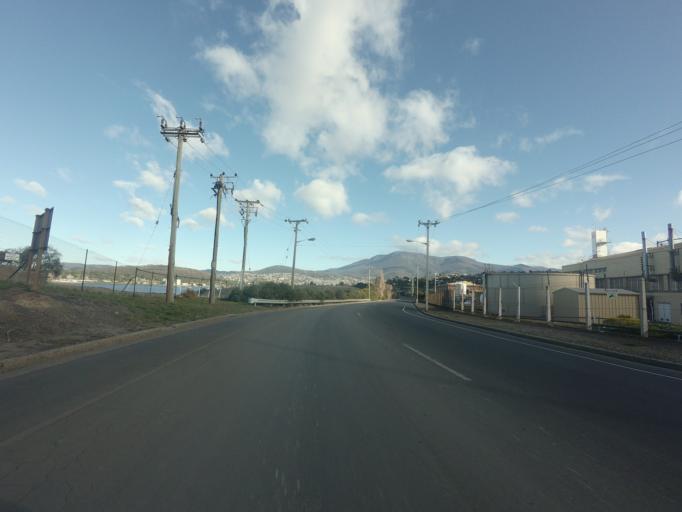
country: AU
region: Tasmania
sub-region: Glenorchy
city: Lutana
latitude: -42.8364
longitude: 147.3218
